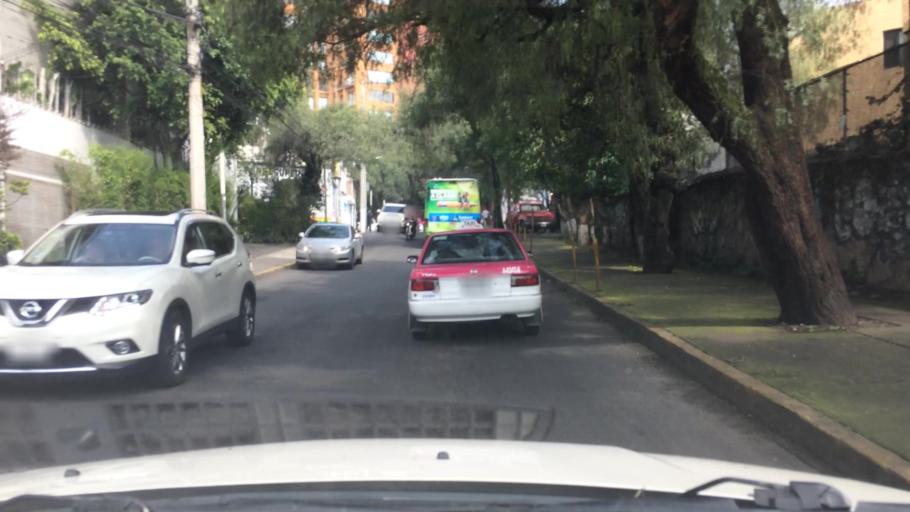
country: MX
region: Mexico City
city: Magdalena Contreras
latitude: 19.3457
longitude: -99.2101
